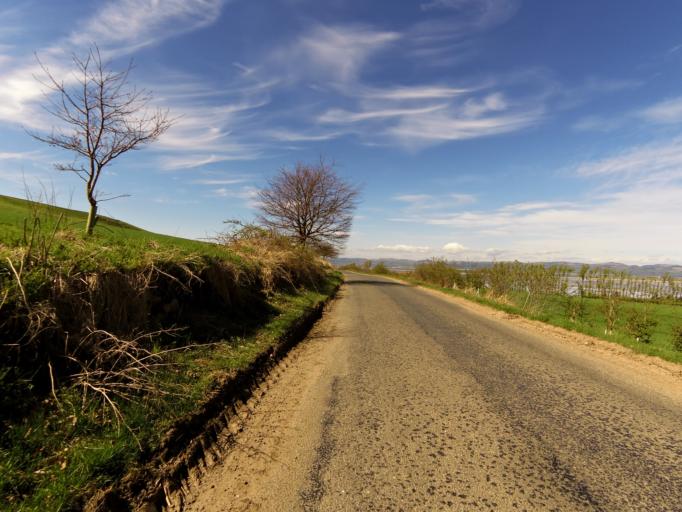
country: GB
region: Scotland
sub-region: Fife
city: Cupar
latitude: 56.3885
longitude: -3.0894
